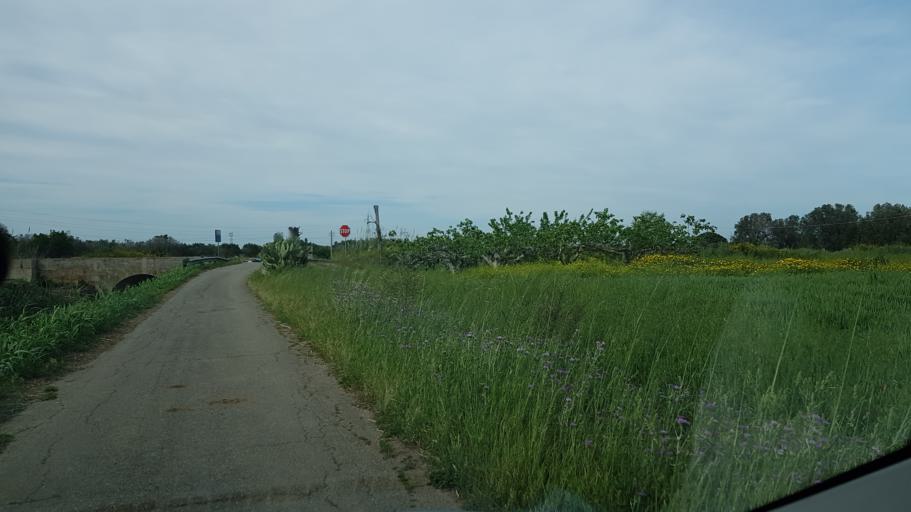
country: IT
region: Apulia
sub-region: Provincia di Brindisi
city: Tuturano
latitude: 40.5457
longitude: 17.9399
